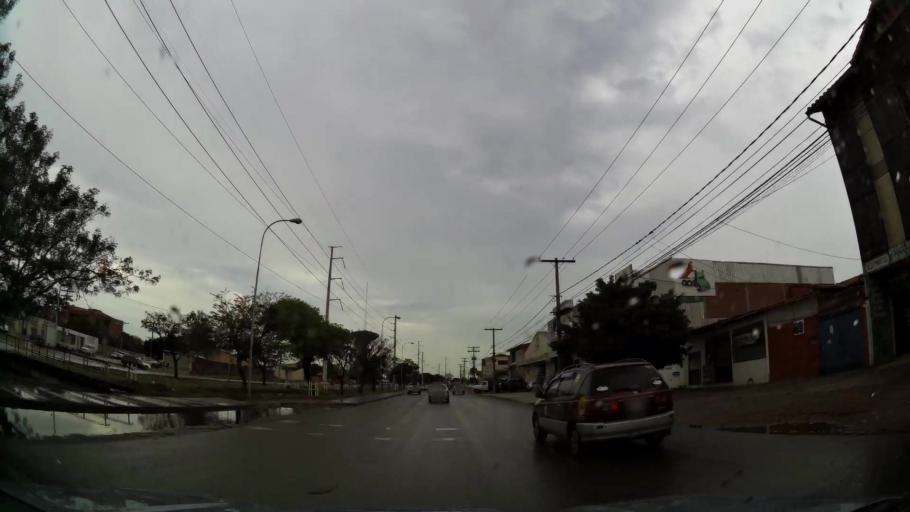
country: BO
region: Santa Cruz
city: Santa Cruz de la Sierra
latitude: -17.7622
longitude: -63.1505
